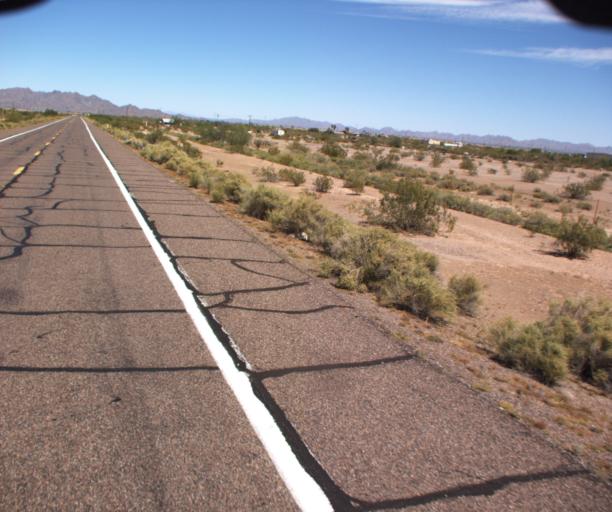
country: US
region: Arizona
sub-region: Maricopa County
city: Gila Bend
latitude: 32.9203
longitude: -112.7348
